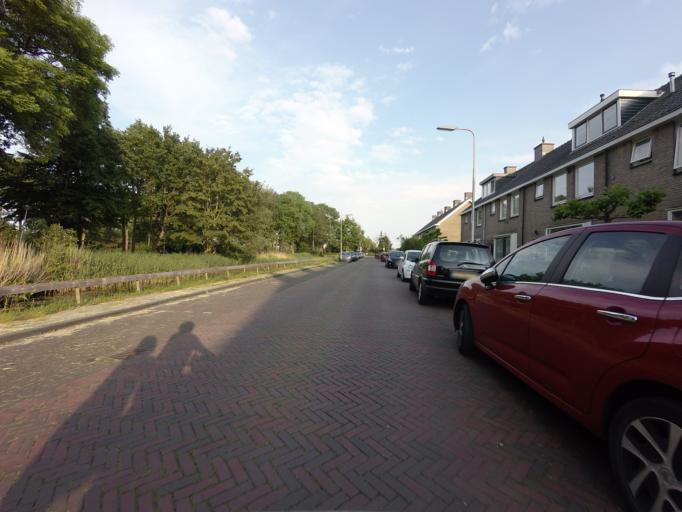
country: NL
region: South Holland
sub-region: Gemeente Lansingerland
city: Bleiswijk
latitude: 52.0130
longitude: 4.5874
